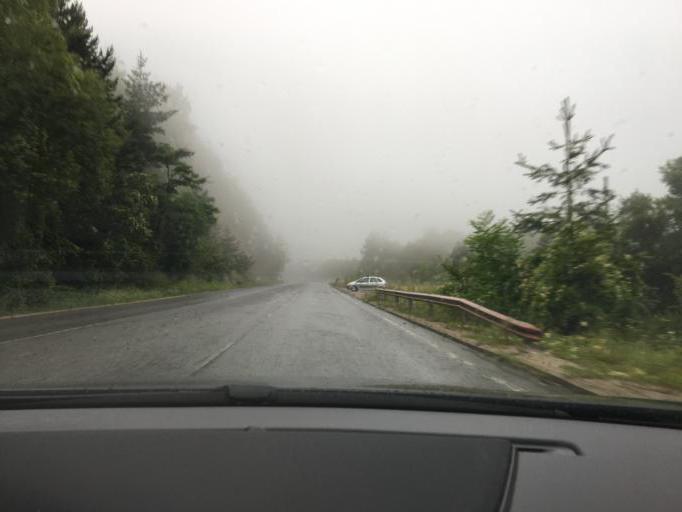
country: MK
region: Kriva Palanka
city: Kriva Palanka
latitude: 42.2176
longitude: 22.4684
